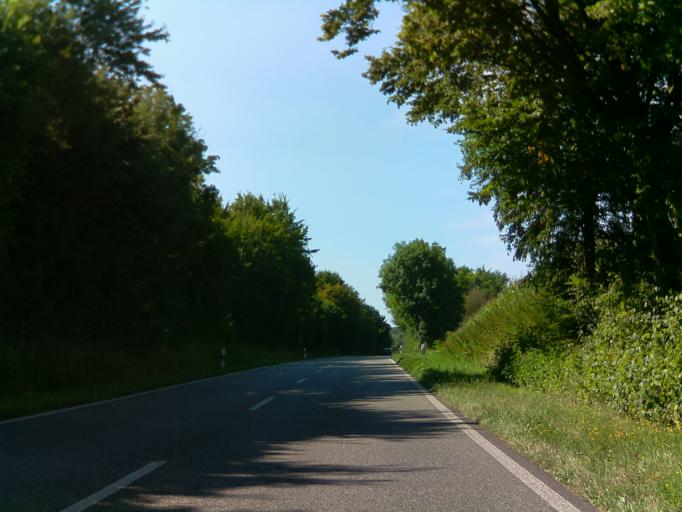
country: DE
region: Baden-Wuerttemberg
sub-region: Karlsruhe Region
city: Oberderdingen
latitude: 49.0942
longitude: 8.7560
